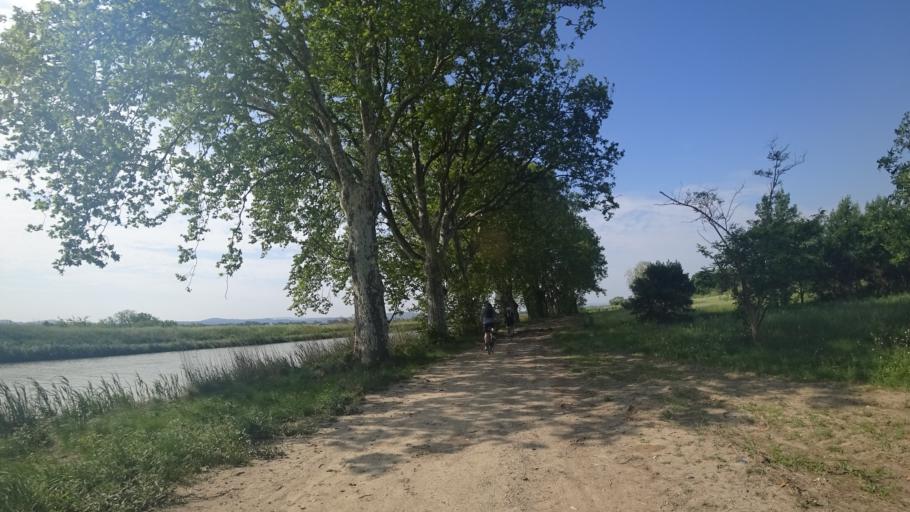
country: FR
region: Languedoc-Roussillon
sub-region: Departement de l'Aude
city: Ginestas
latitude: 43.2549
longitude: 2.8860
